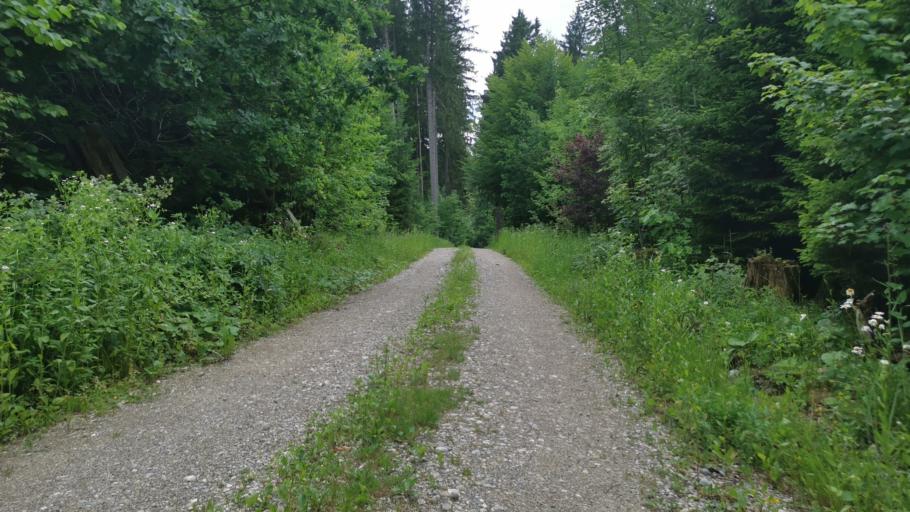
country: DE
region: Bavaria
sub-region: Upper Bavaria
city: Schaftlarn
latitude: 48.0089
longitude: 11.4671
